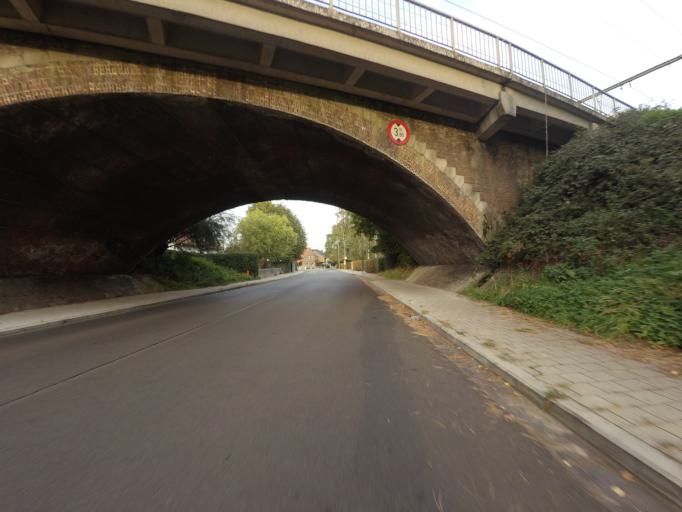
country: BE
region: Flanders
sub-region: Provincie Oost-Vlaanderen
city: Destelbergen
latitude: 51.0734
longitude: 3.7680
